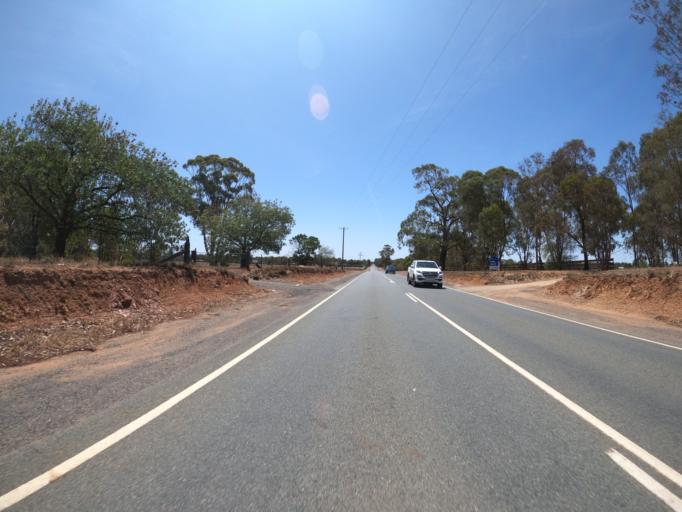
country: AU
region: Victoria
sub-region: Moira
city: Yarrawonga
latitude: -36.0452
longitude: 145.9955
